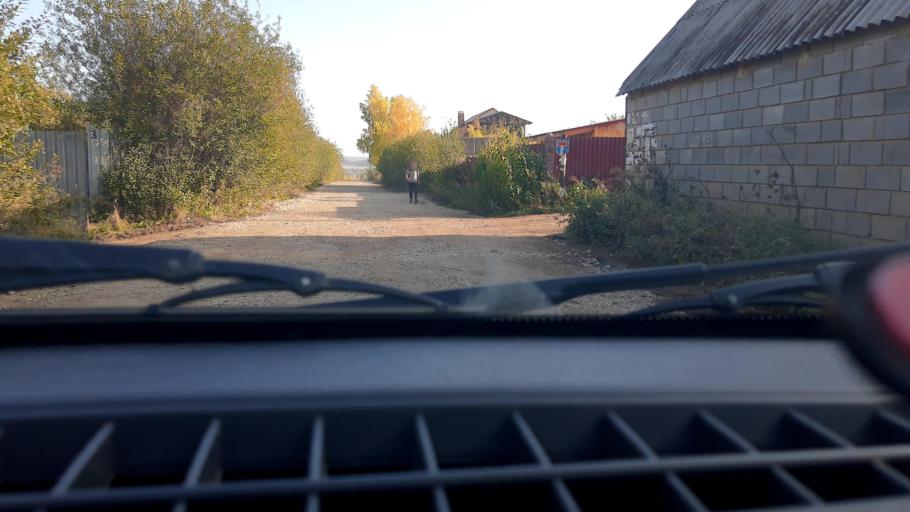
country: RU
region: Bashkortostan
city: Avdon
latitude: 54.5762
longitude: 55.7318
